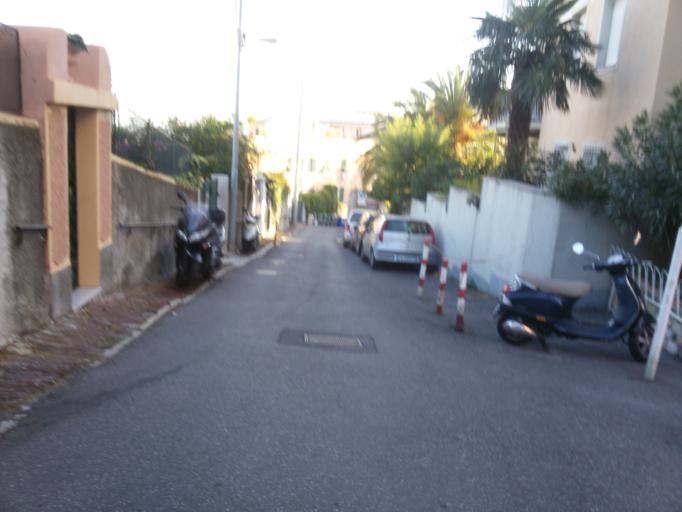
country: IT
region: Liguria
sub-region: Provincia di Genova
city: Genoa
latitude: 44.4103
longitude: 8.9782
